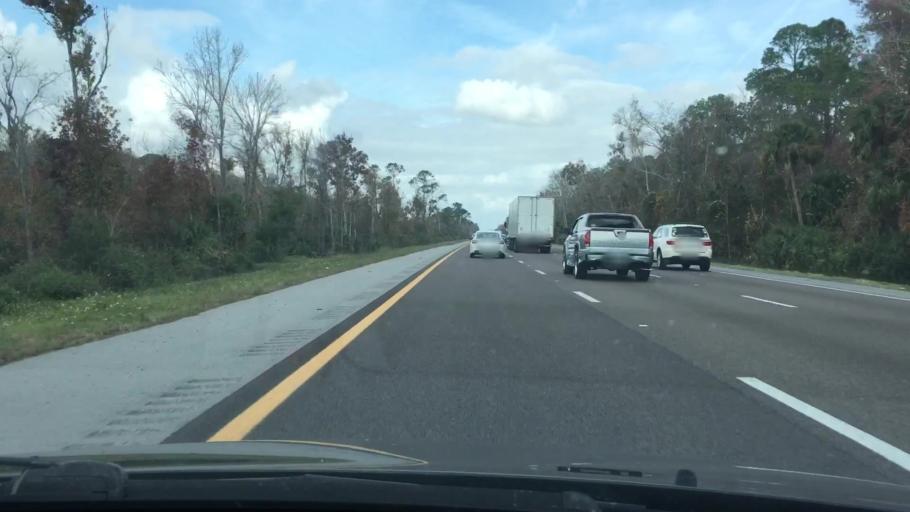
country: US
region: Florida
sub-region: Volusia County
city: Oak Hill
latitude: 28.9031
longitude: -80.9319
